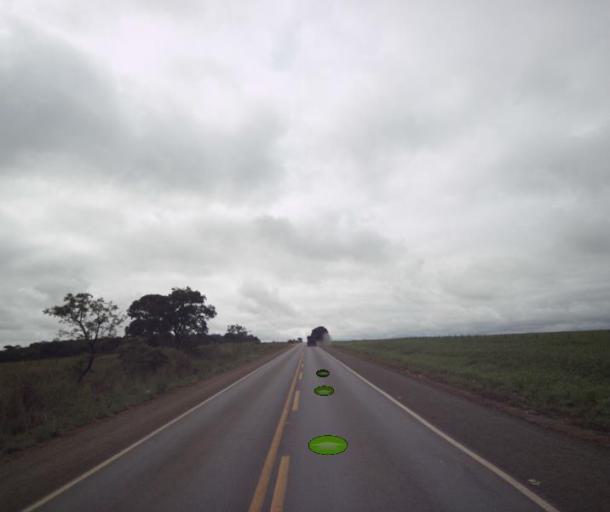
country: BR
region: Goias
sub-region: Uruacu
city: Uruacu
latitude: -14.6597
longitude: -49.1577
